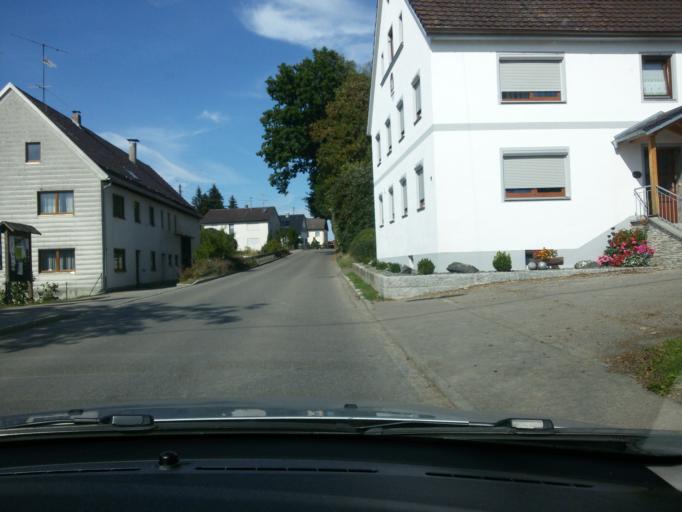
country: DE
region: Bavaria
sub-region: Swabia
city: Mickhausen
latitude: 48.2671
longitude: 10.6485
